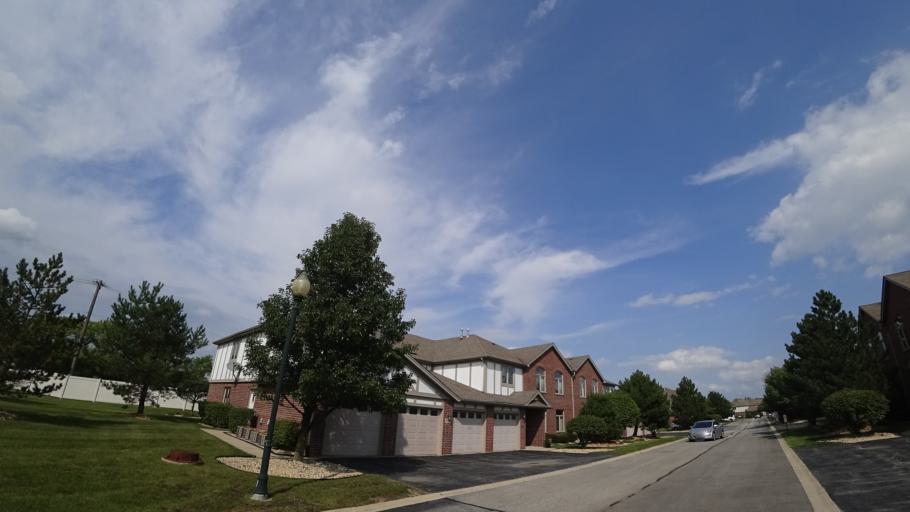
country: US
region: Illinois
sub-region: Cook County
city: Tinley Park
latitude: 41.5584
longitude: -87.7705
